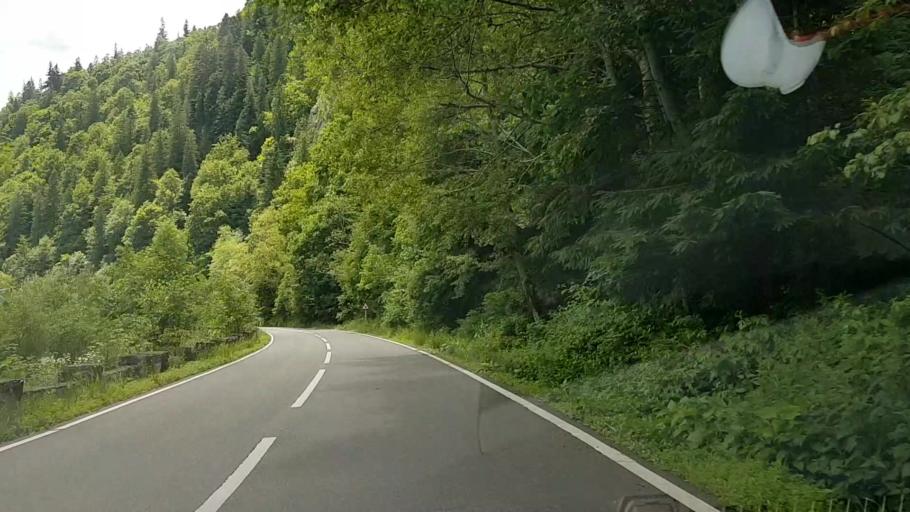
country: RO
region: Suceava
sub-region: Comuna Crucea
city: Crucea
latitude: 47.3166
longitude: 25.6254
